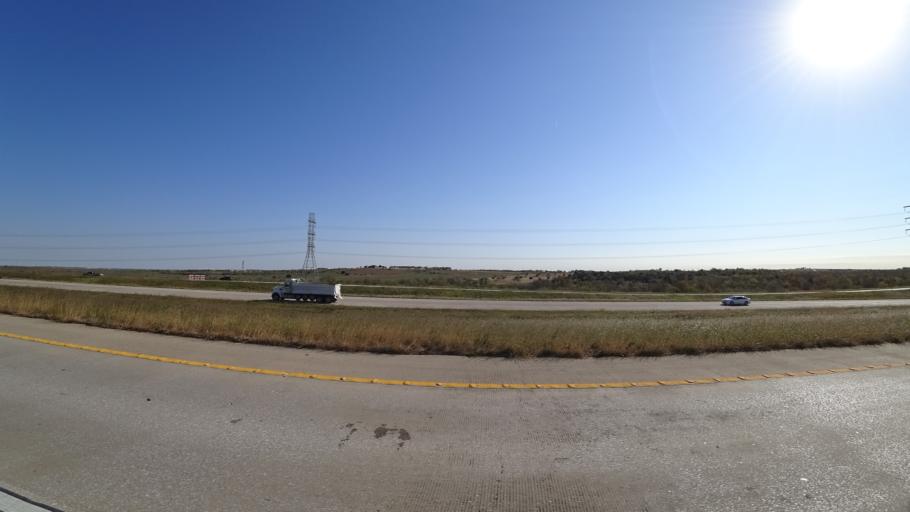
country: US
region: Texas
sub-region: Travis County
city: Garfield
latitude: 30.1200
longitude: -97.6603
